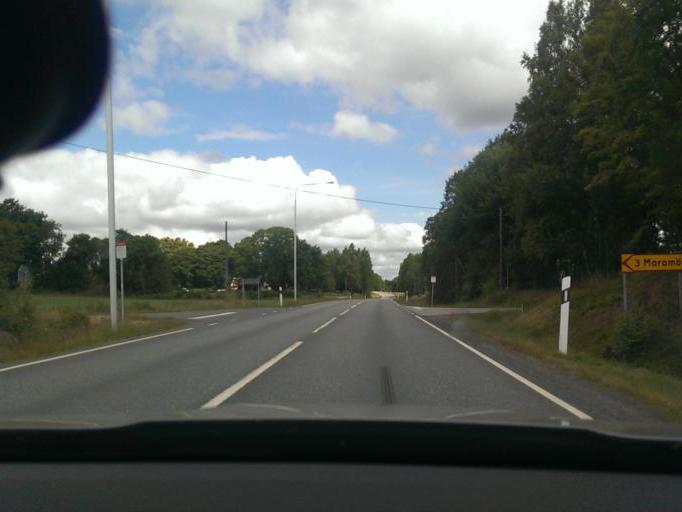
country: SE
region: Joenkoeping
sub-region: Varnamo Kommun
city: Varnamo
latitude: 57.2323
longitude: 14.0059
